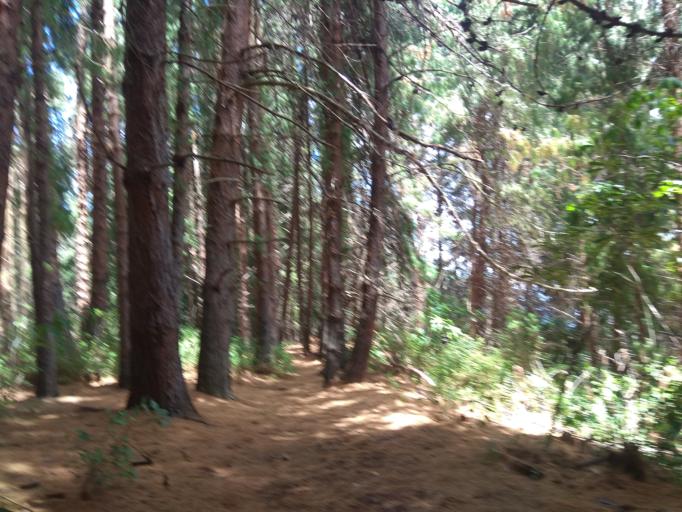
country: CR
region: Cartago
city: Cot
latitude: 9.9559
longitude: -83.8748
